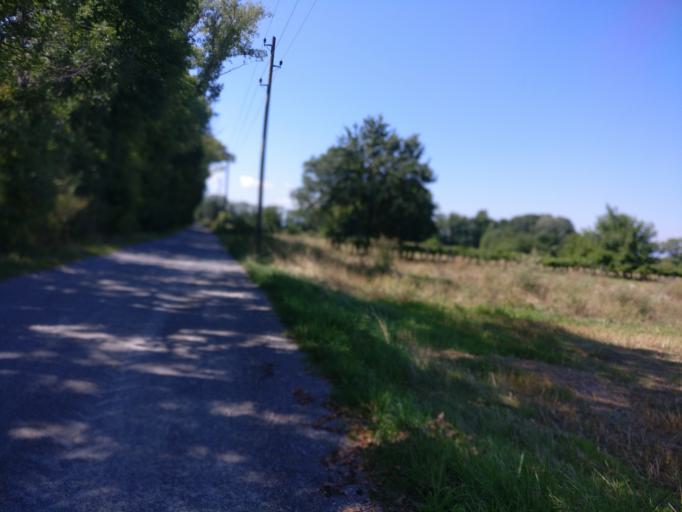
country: AT
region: Lower Austria
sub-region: Politischer Bezirk Baden
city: Pottendorf
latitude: 47.9082
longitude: 16.3530
